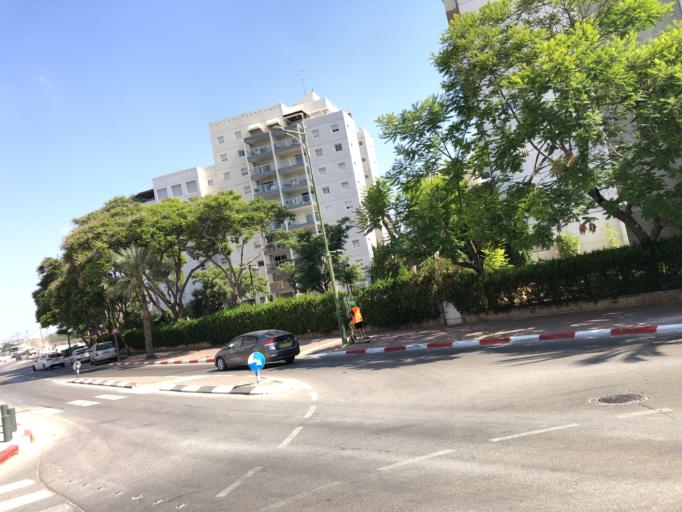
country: IL
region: Central District
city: Yehud
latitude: 32.0302
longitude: 34.8790
